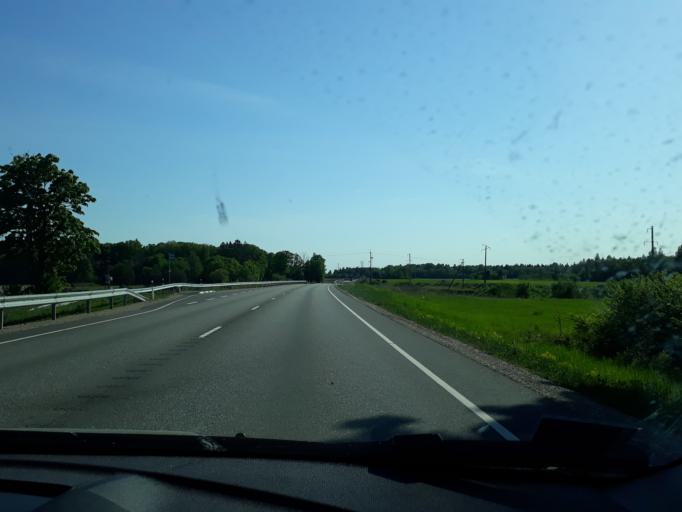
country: EE
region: Paernumaa
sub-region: Tootsi vald
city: Tootsi
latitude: 58.5783
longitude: 24.8879
